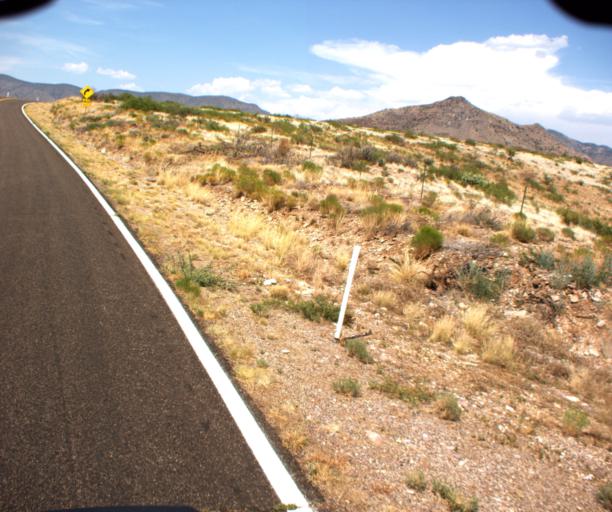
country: US
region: Arizona
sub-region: Greenlee County
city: Clifton
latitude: 33.0051
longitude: -109.1613
